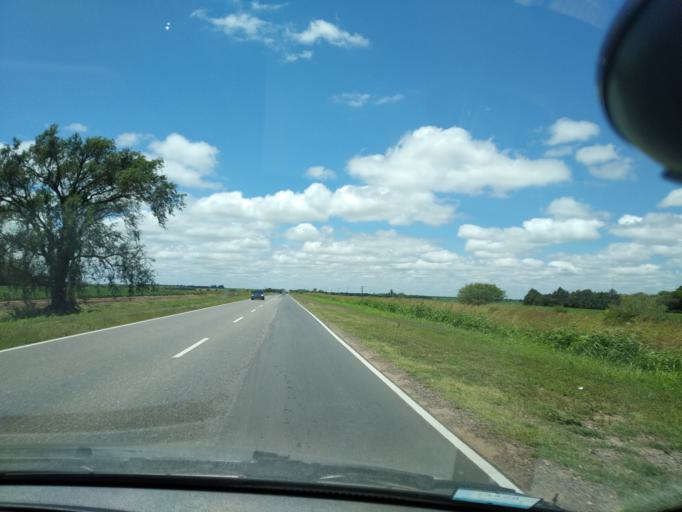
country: AR
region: Cordoba
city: Despenaderos
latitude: -31.6511
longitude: -64.1835
